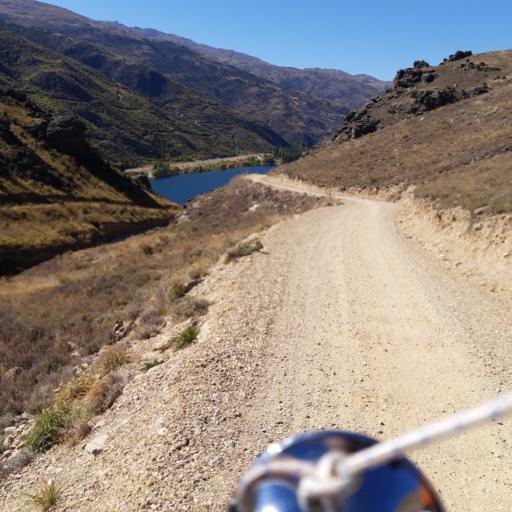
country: NZ
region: Otago
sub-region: Queenstown-Lakes District
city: Wanaka
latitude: -45.0844
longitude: 169.2456
